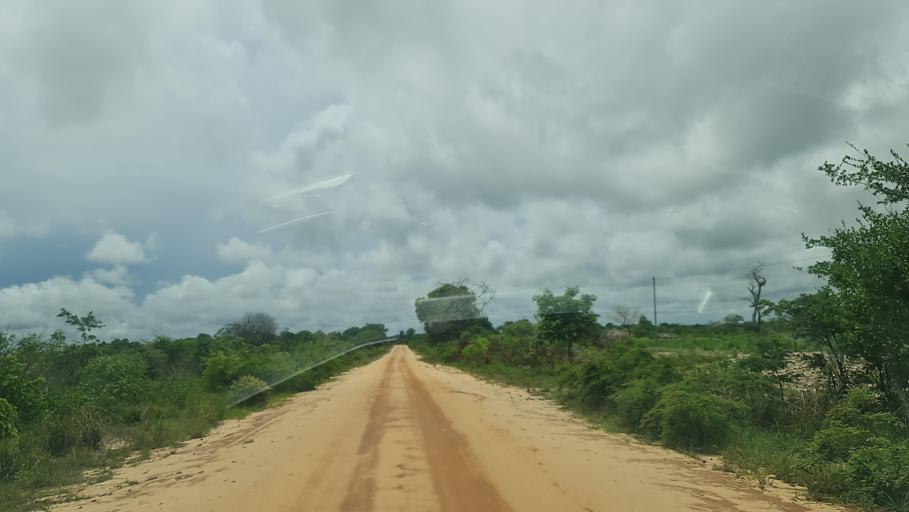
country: MZ
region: Zambezia
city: Quelimane
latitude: -17.2637
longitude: 37.2379
